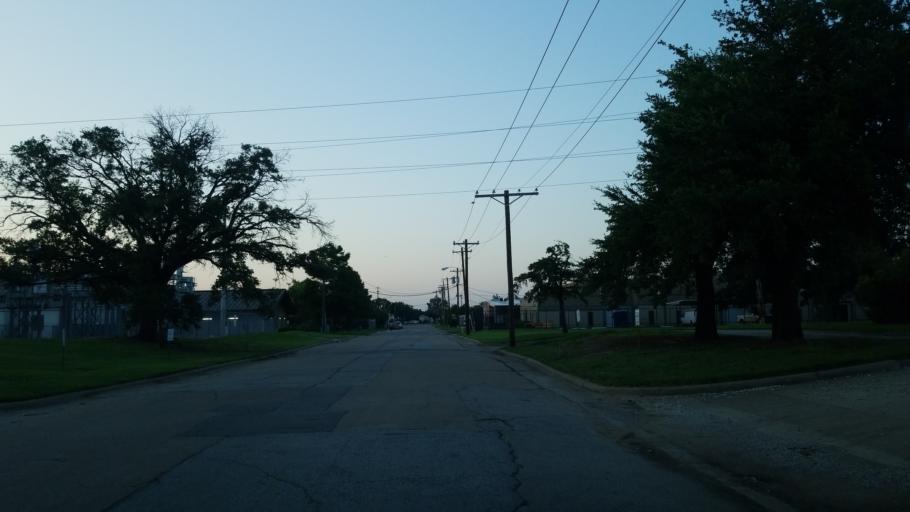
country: US
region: Texas
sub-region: Dallas County
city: Farmers Branch
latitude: 32.8828
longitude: -96.8927
